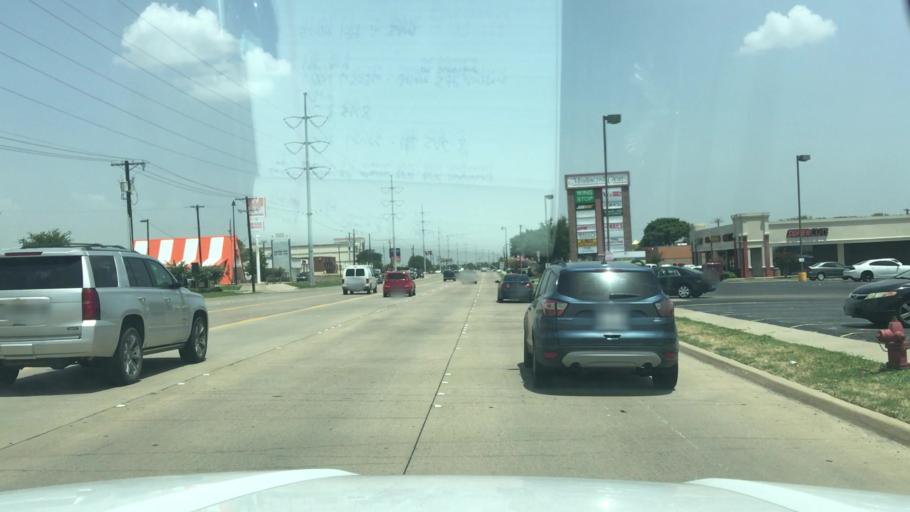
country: US
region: Texas
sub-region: Tarrant County
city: North Richland Hills
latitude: 32.8459
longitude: -97.2385
